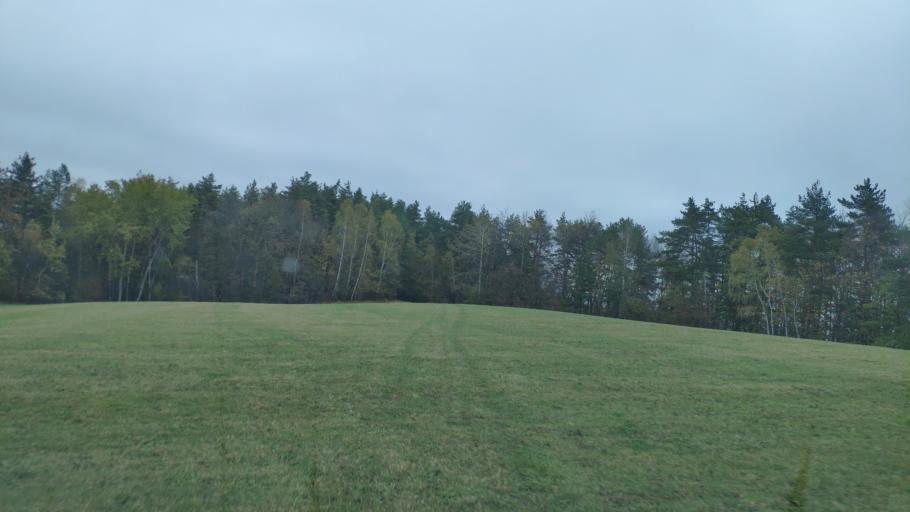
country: SK
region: Presovsky
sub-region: Okres Presov
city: Presov
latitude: 48.9376
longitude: 21.1026
